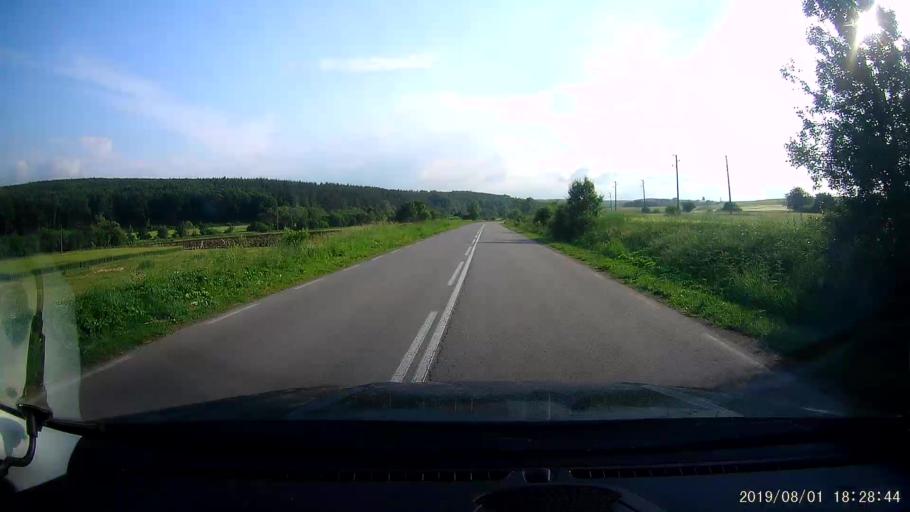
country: BG
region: Shumen
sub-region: Obshtina Venets
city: Venets
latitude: 43.5708
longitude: 26.9579
